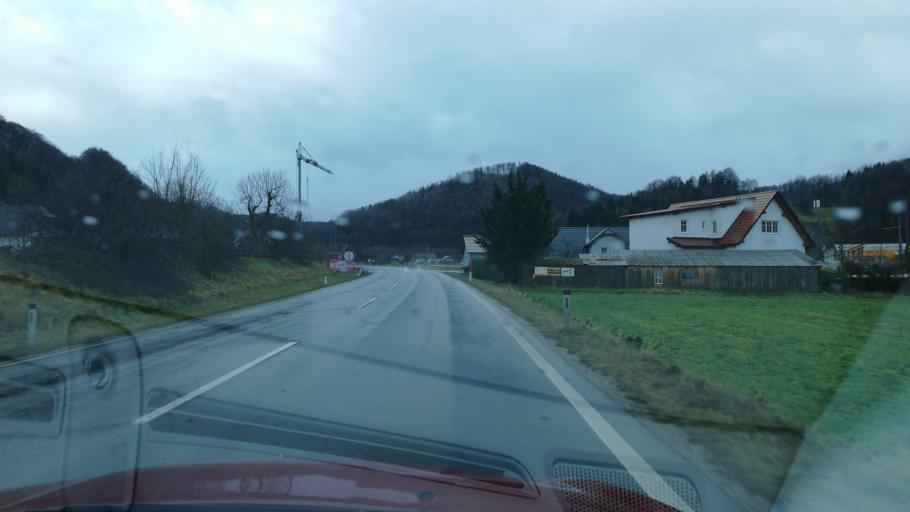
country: AT
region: Upper Austria
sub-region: Politischer Bezirk Kirchdorf an der Krems
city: Micheldorf in Oberoesterreich
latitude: 47.8730
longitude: 14.1322
